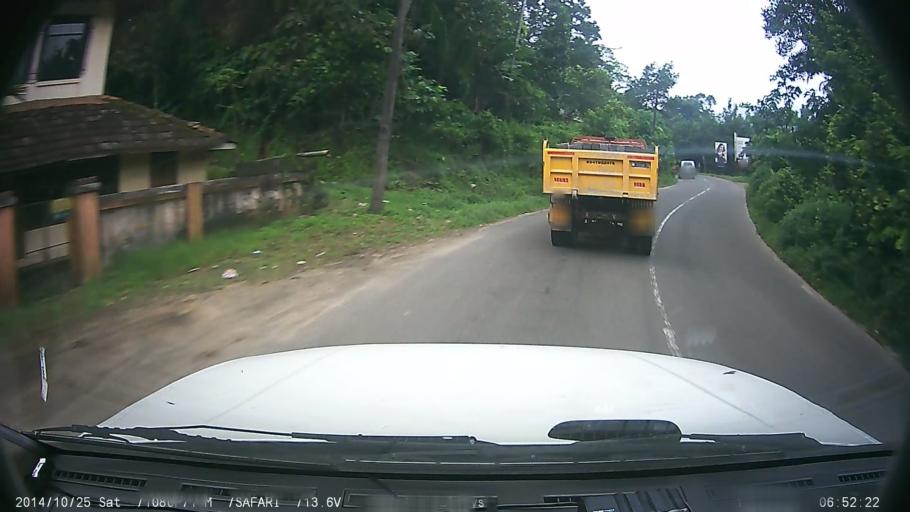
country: IN
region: Kerala
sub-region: Ernakulam
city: Muvattupuzha
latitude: 9.9181
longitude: 76.5827
